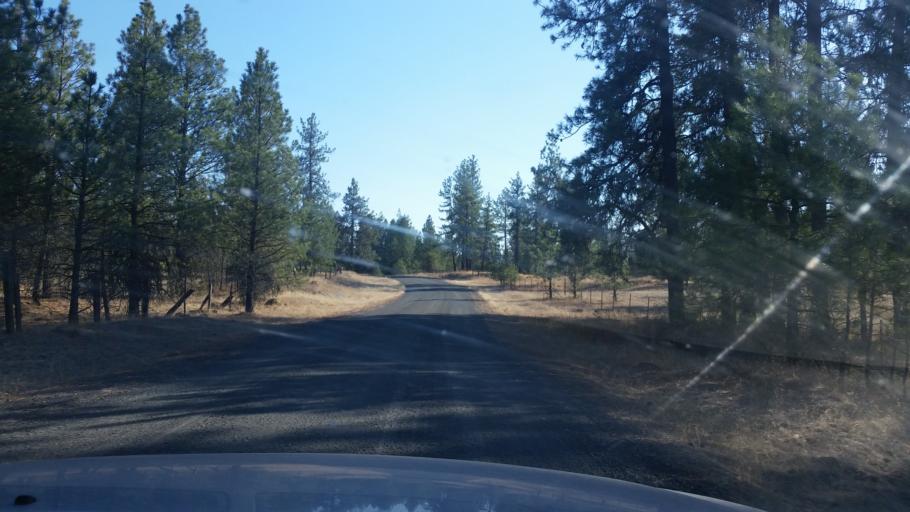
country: US
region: Washington
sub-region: Spokane County
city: Cheney
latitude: 47.4214
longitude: -117.6500
